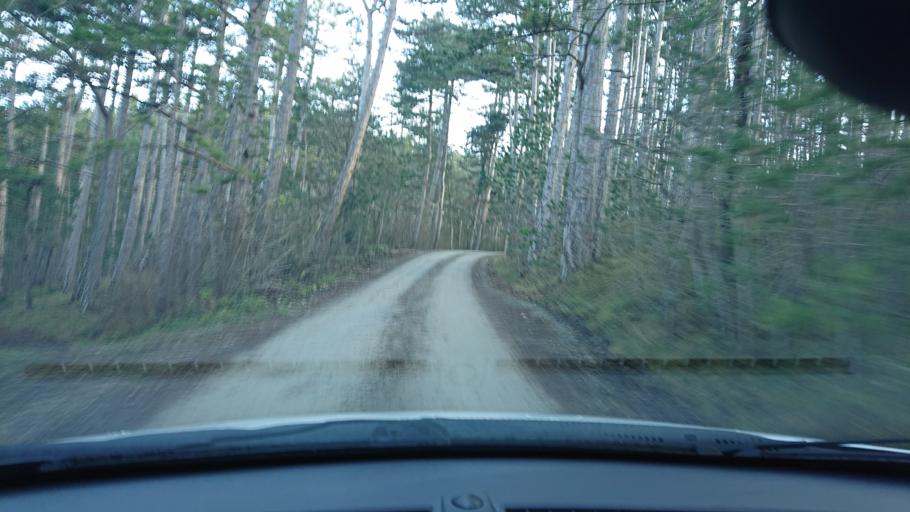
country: AT
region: Lower Austria
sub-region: Politischer Bezirk Baden
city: Berndorf
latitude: 47.9298
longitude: 16.1018
